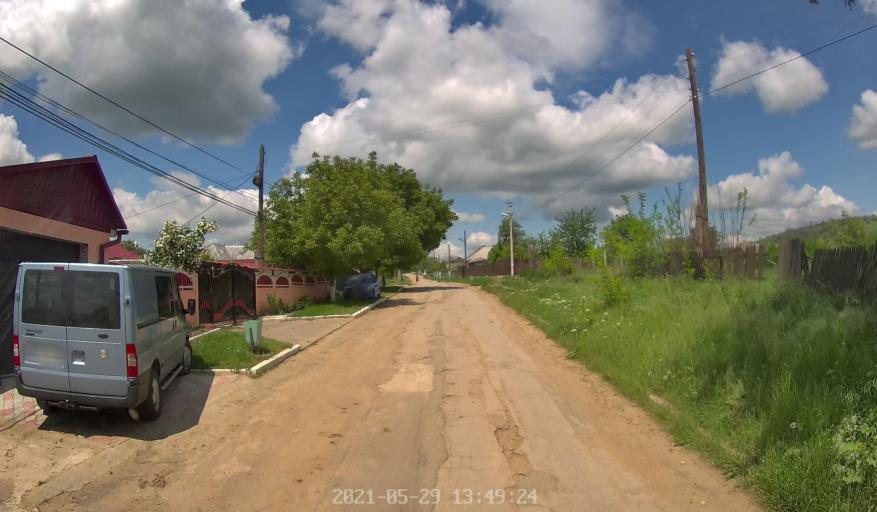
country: MD
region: Hincesti
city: Hincesti
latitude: 46.8360
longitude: 28.6769
